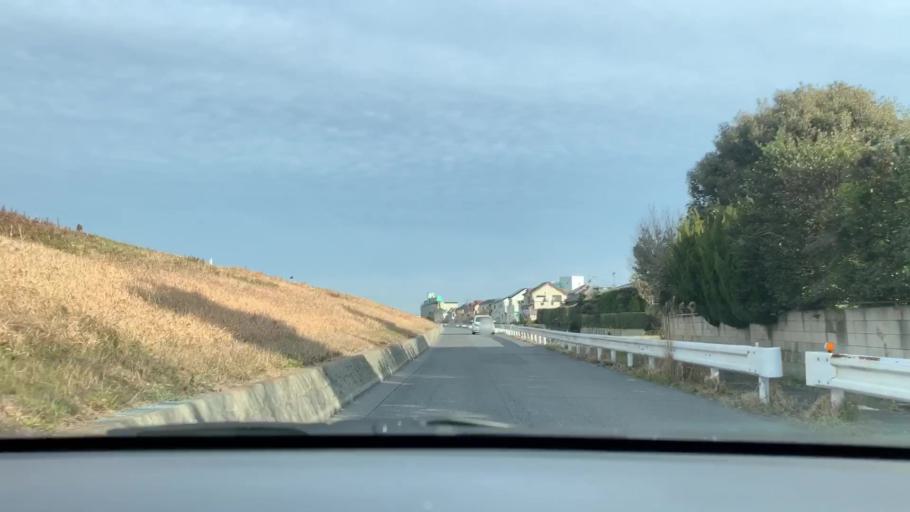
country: JP
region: Chiba
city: Matsudo
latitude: 35.8110
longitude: 139.8923
